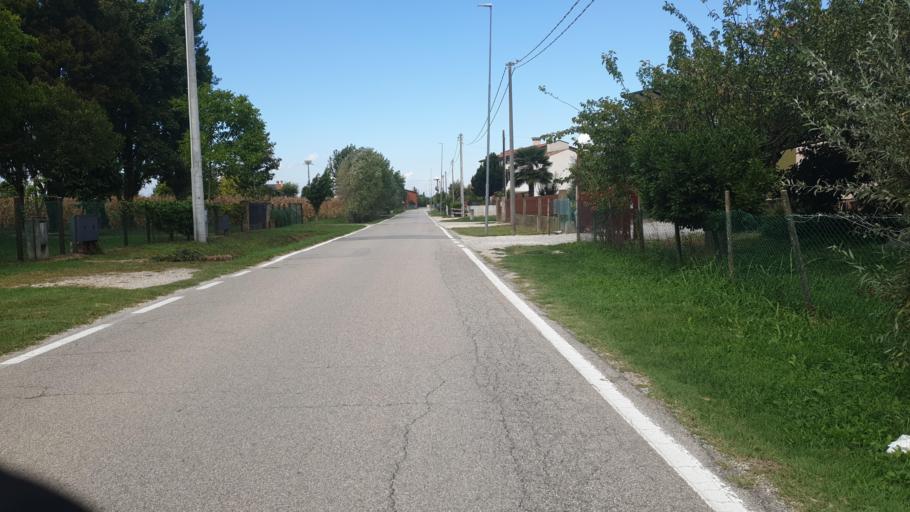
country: IT
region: Veneto
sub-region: Provincia di Padova
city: Terradura
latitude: 45.3379
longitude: 11.8123
